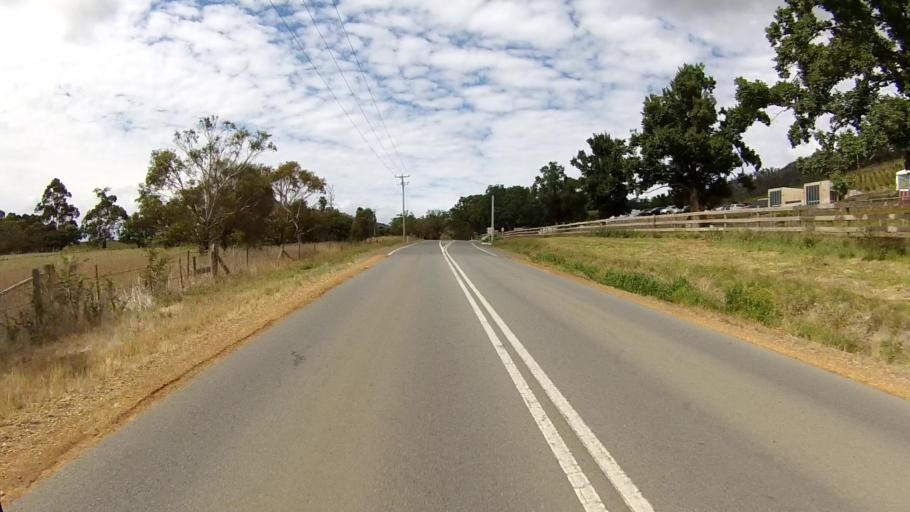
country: AU
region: Tasmania
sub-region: Clarence
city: Cambridge
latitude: -42.8022
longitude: 147.4227
